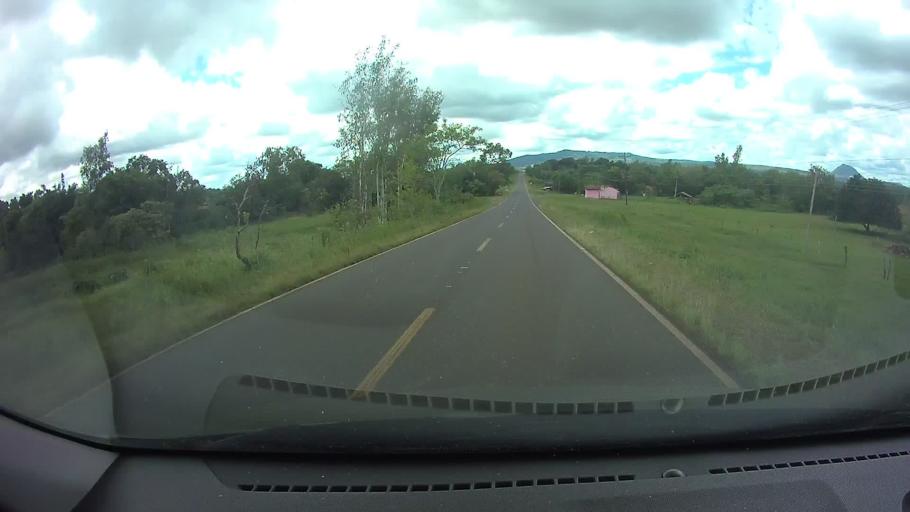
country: PY
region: Paraguari
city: Ybycui
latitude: -25.9131
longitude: -57.0459
